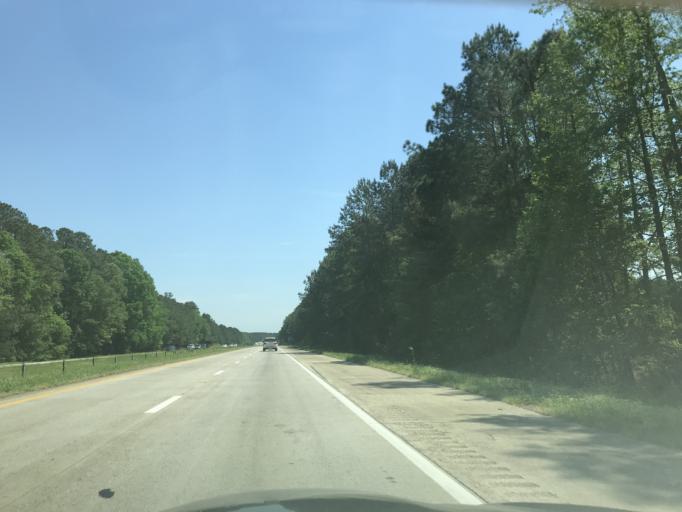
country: US
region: North Carolina
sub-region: Johnston County
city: Benson
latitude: 35.5286
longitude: -78.5667
